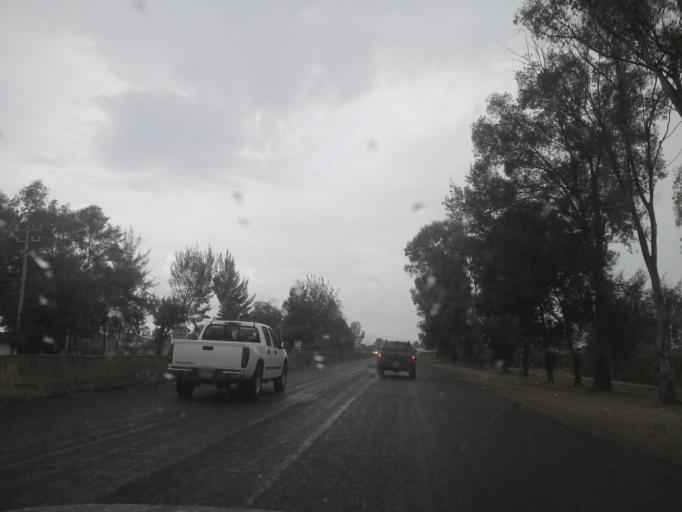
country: MX
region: Jalisco
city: Arandas
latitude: 20.7086
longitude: -102.3892
